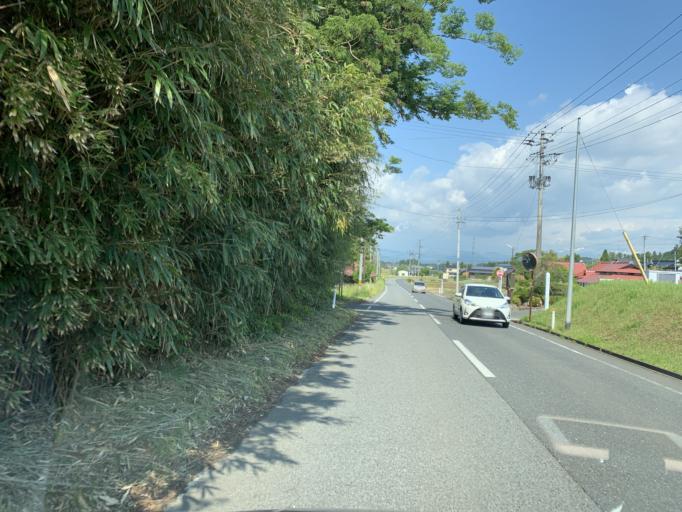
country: JP
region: Iwate
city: Ichinoseki
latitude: 38.7968
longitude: 141.0209
